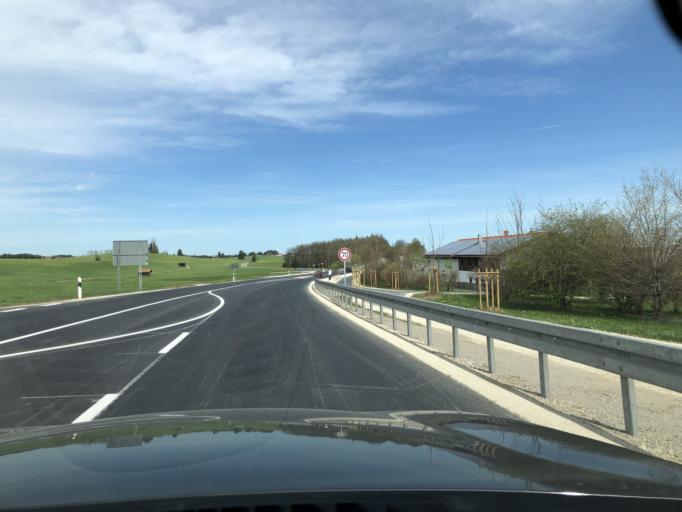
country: DE
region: Bavaria
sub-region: Swabia
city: Seeg
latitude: 47.6590
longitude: 10.6086
